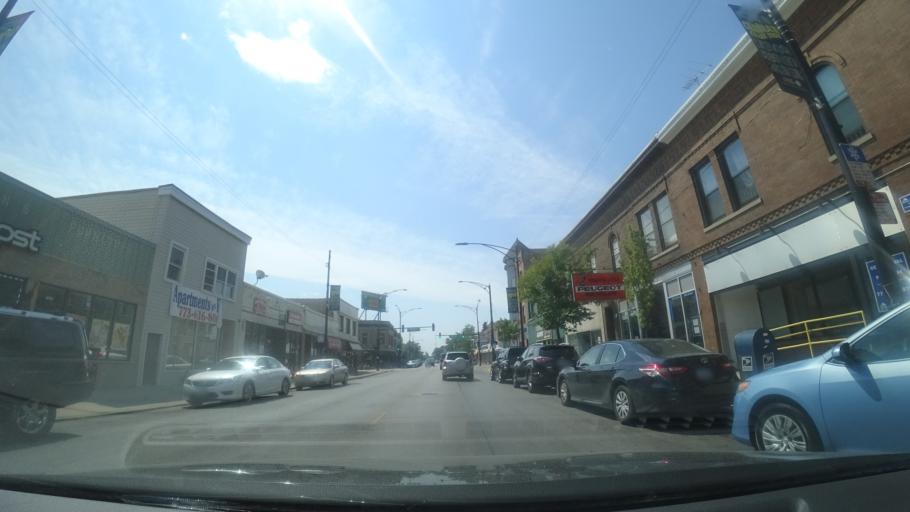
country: US
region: Illinois
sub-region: Cook County
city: Evanston
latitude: 42.0107
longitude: -87.6744
